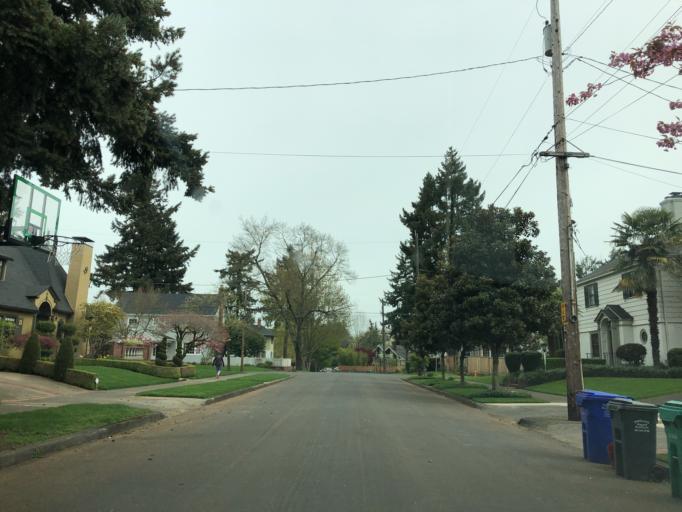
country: US
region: Oregon
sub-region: Multnomah County
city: Portland
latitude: 45.5494
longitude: -122.6325
